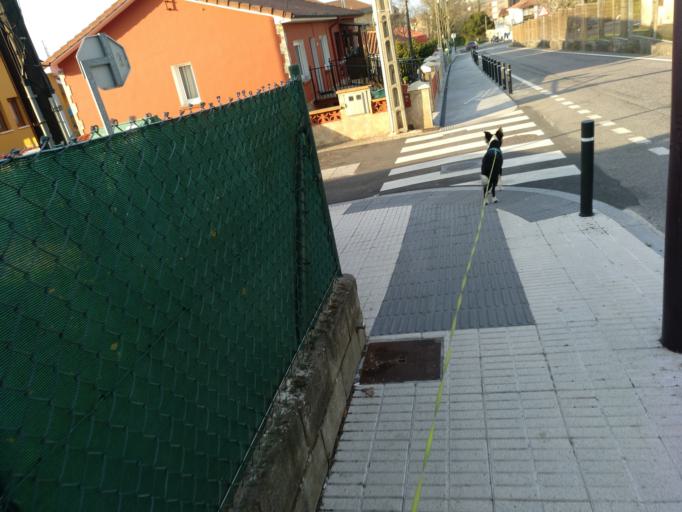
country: ES
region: Asturias
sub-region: Province of Asturias
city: Gijon
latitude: 43.5161
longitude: -5.6636
